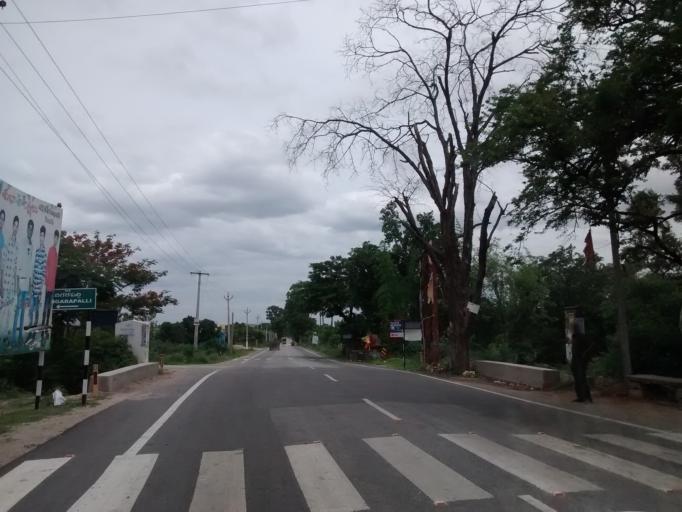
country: IN
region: Andhra Pradesh
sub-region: Chittoor
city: Chittoor
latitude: 13.2937
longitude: 79.0384
